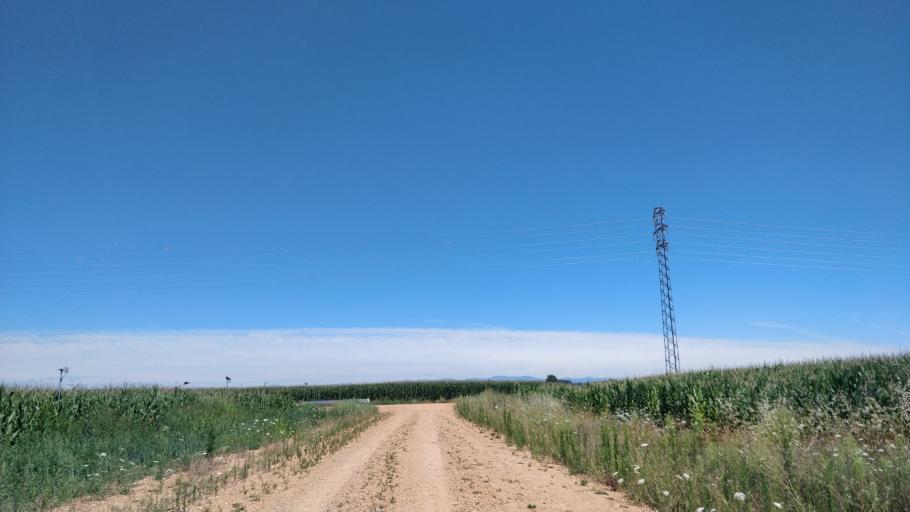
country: ES
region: Castille and Leon
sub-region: Provincia de Leon
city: Bustillo del Paramo
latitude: 42.4597
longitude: -5.8166
